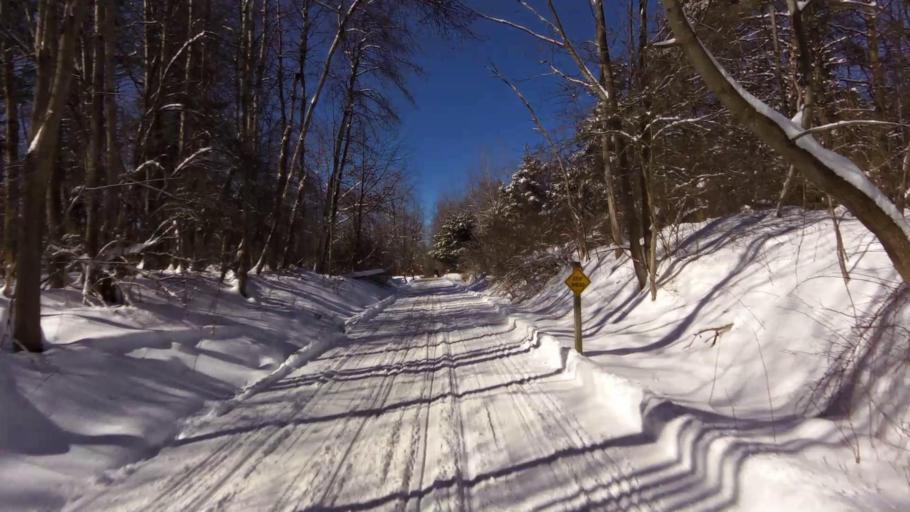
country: US
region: New York
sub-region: Chautauqua County
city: Mayville
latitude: 42.2361
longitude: -79.5102
